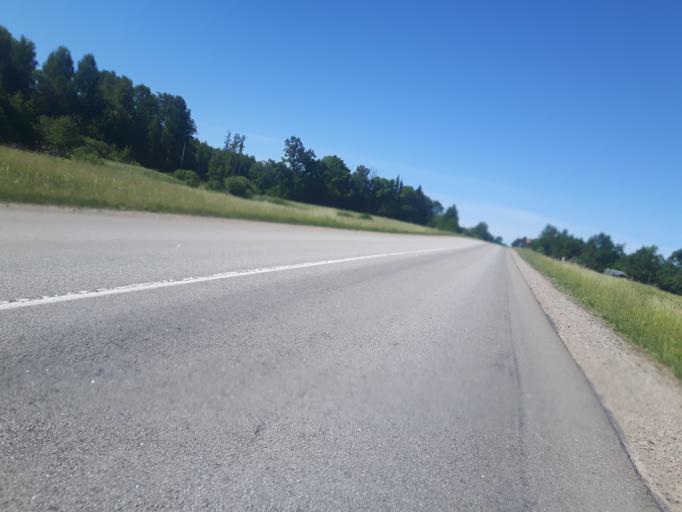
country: LV
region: Durbe
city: Liegi
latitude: 56.6889
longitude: 21.4099
